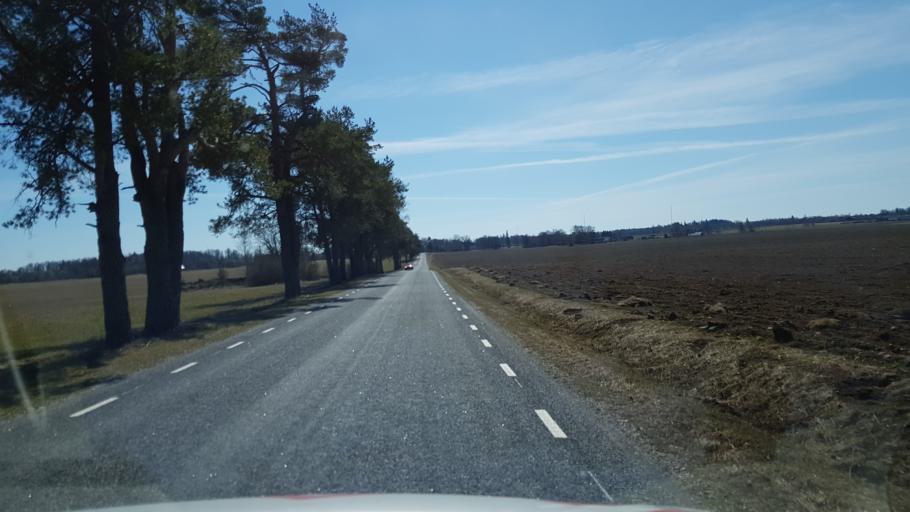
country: EE
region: Laeaene-Virumaa
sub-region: Vinni vald
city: Vinni
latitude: 59.1079
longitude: 26.5250
